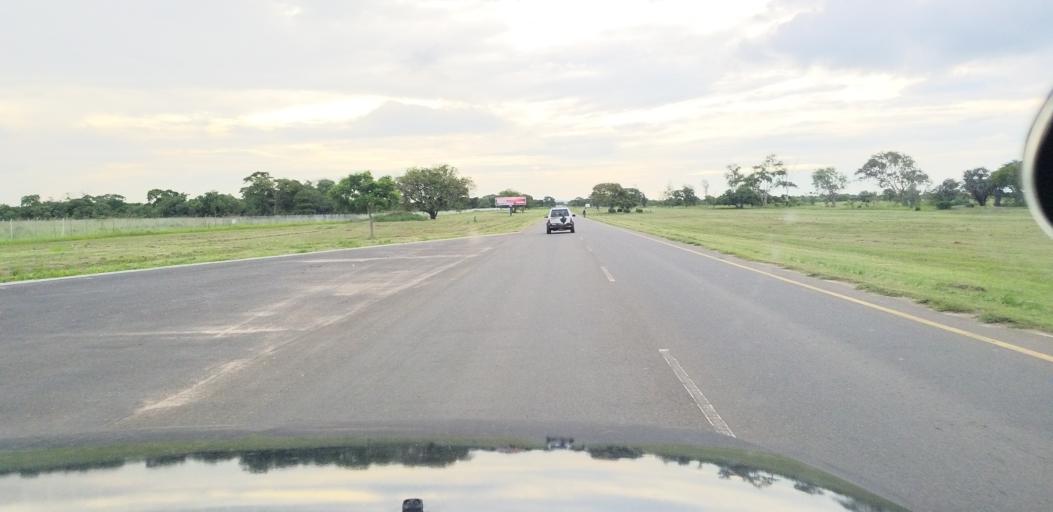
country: ZM
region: Lusaka
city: Lusaka
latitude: -15.3196
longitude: 28.4352
